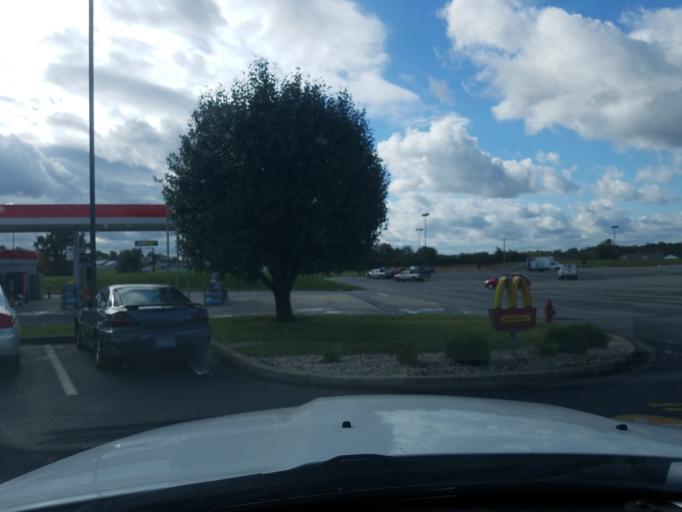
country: US
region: Kentucky
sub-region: Russell County
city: Russell Springs
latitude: 37.0621
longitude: -85.0716
